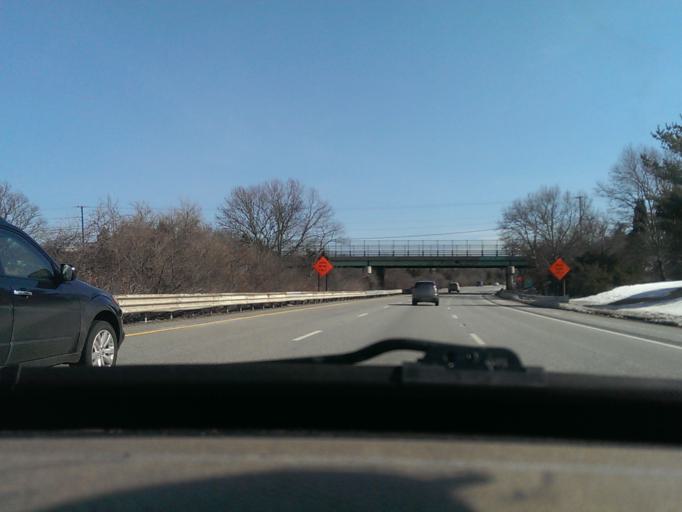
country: US
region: Massachusetts
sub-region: Bristol County
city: Swansea
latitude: 41.7294
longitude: -71.1897
